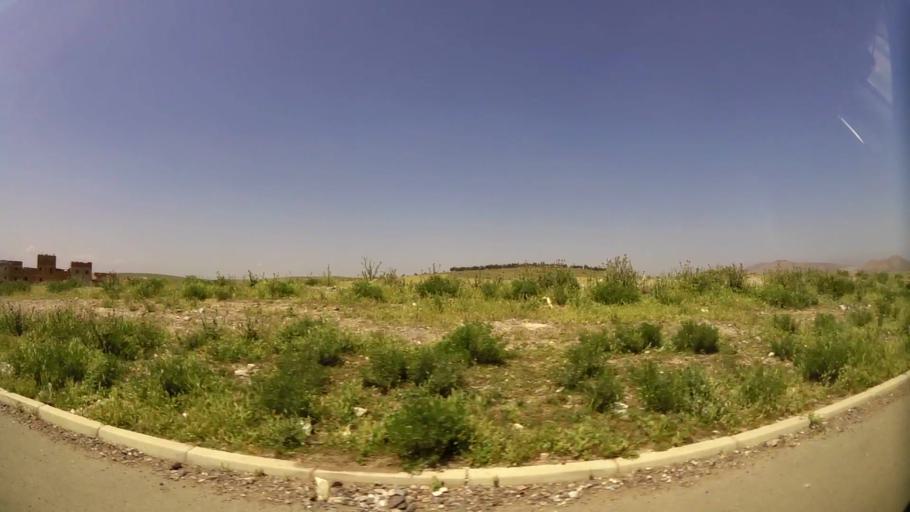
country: MA
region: Oriental
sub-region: Oujda-Angad
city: Oujda
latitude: 34.6808
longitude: -1.9601
